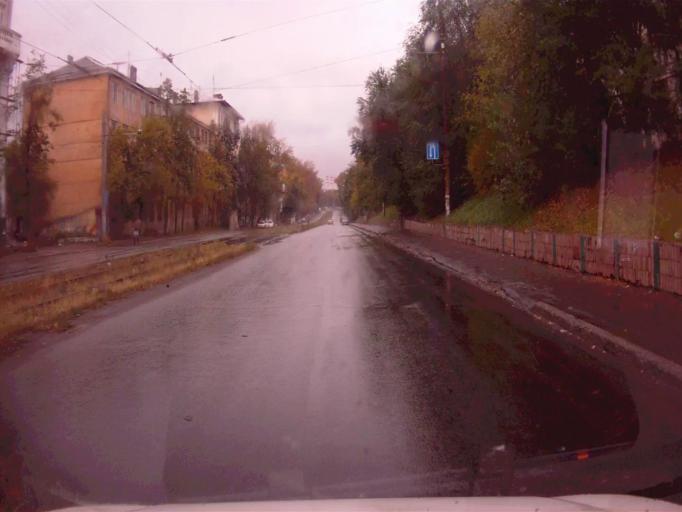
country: RU
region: Chelyabinsk
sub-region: Gorod Chelyabinsk
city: Chelyabinsk
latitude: 55.1859
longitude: 61.4140
